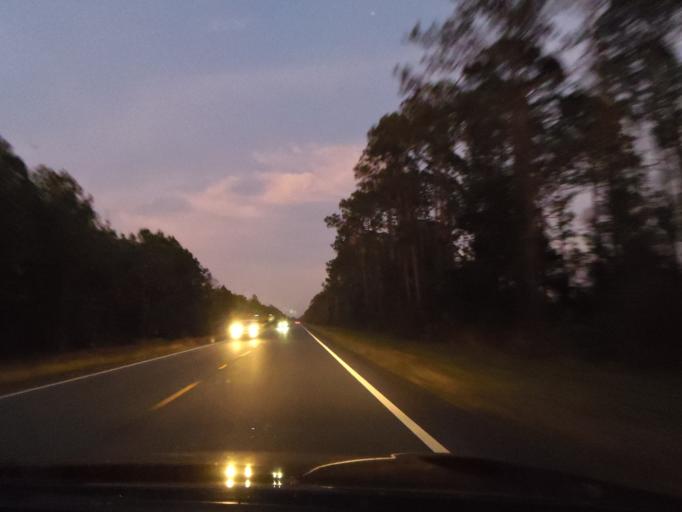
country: US
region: Florida
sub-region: Volusia County
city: De Leon Springs
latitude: 29.2336
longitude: -81.2785
